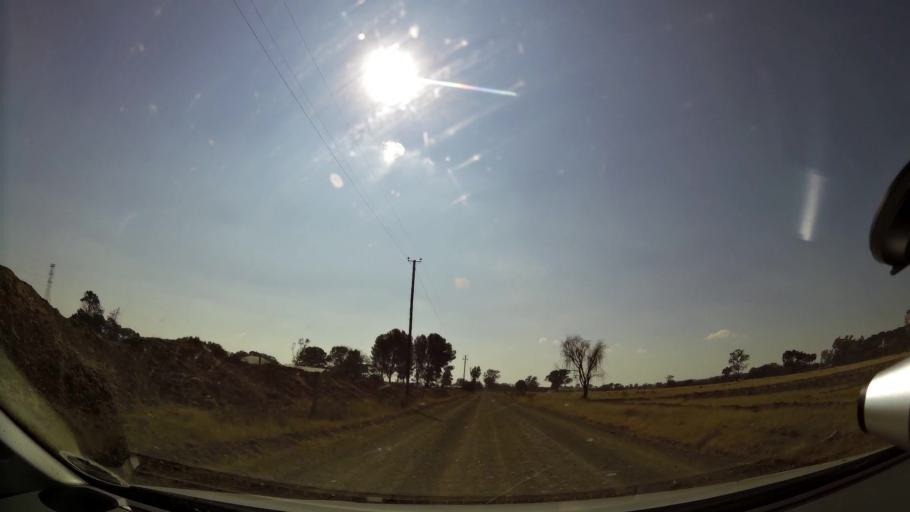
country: ZA
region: Orange Free State
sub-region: Mangaung Metropolitan Municipality
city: Bloemfontein
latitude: -29.1701
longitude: 26.3084
